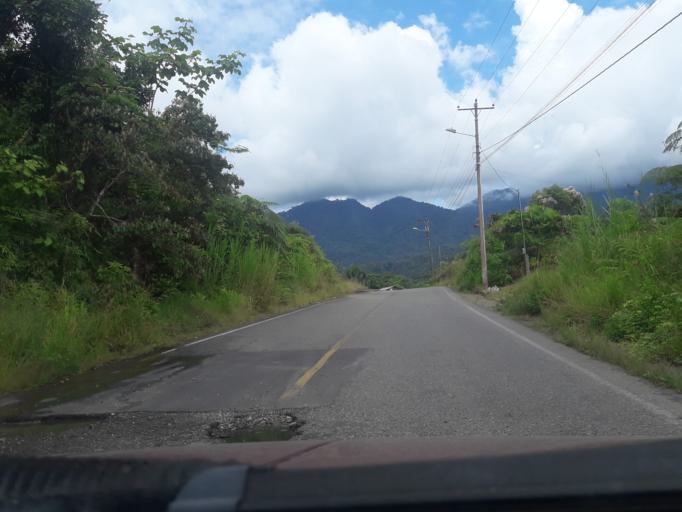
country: EC
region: Napo
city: Tena
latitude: -1.0252
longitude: -77.8850
